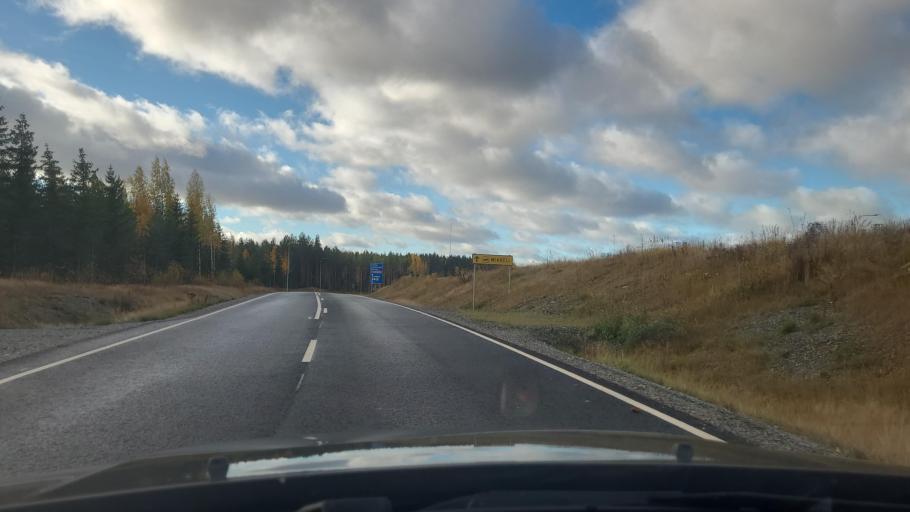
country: FI
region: Southern Savonia
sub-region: Pieksaemaeki
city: Juva
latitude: 61.8326
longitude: 27.6590
